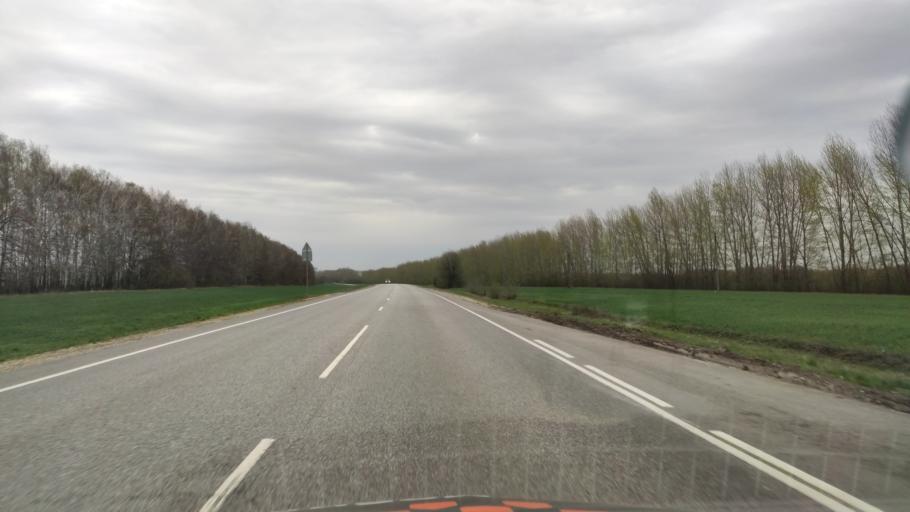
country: RU
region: Kursk
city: Olym
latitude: 51.5509
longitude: 38.2050
